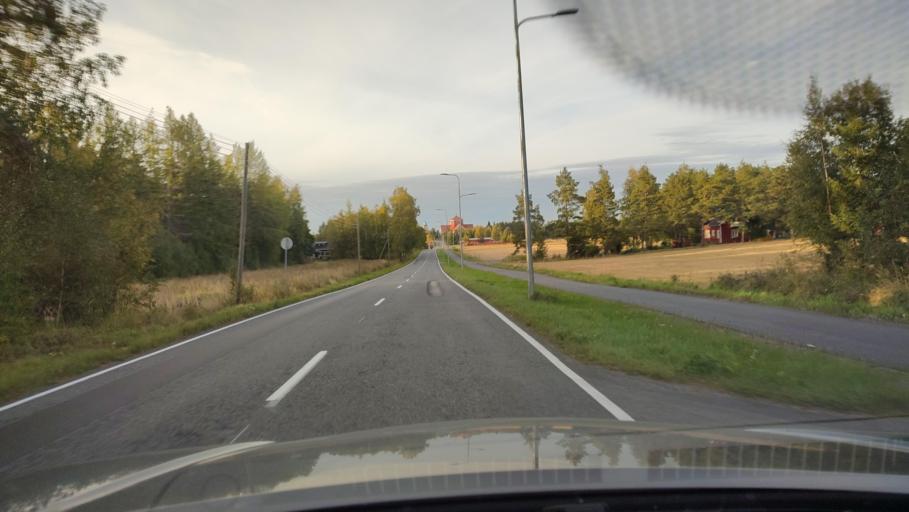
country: FI
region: Ostrobothnia
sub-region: Sydosterbotten
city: Kristinestad
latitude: 62.2378
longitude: 21.5209
